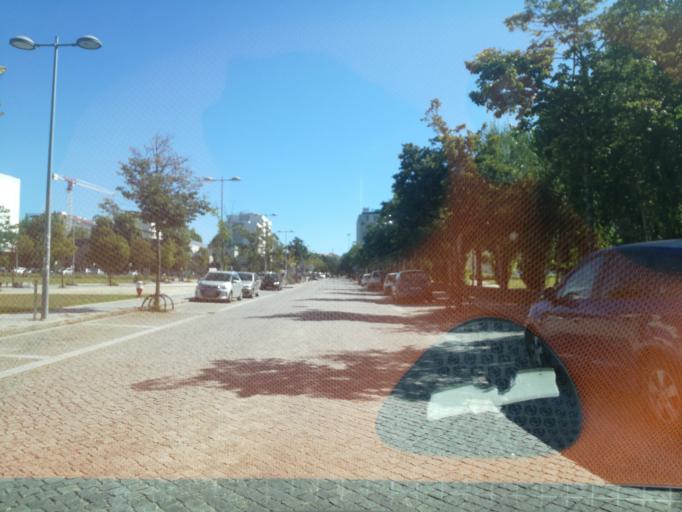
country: PT
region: Porto
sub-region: Matosinhos
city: Sao Mamede de Infesta
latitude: 41.1759
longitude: -8.6039
